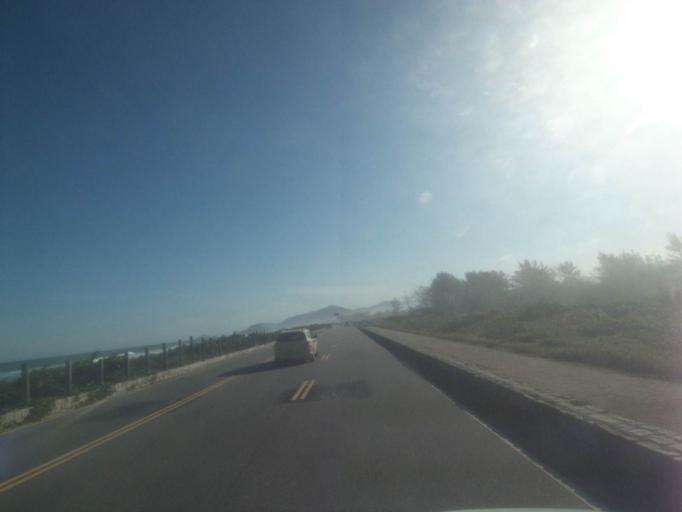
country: BR
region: Rio de Janeiro
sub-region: Nilopolis
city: Nilopolis
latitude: -23.0166
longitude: -43.4203
